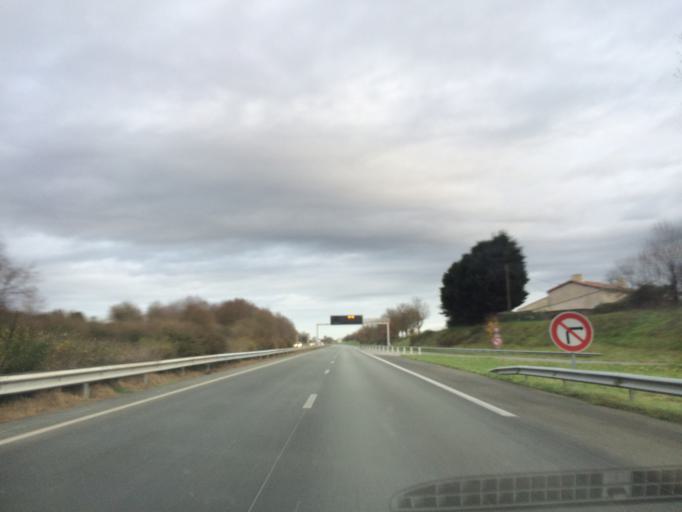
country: FR
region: Poitou-Charentes
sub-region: Departement des Deux-Sevres
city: Nanteuil
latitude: 46.4150
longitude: -0.1199
